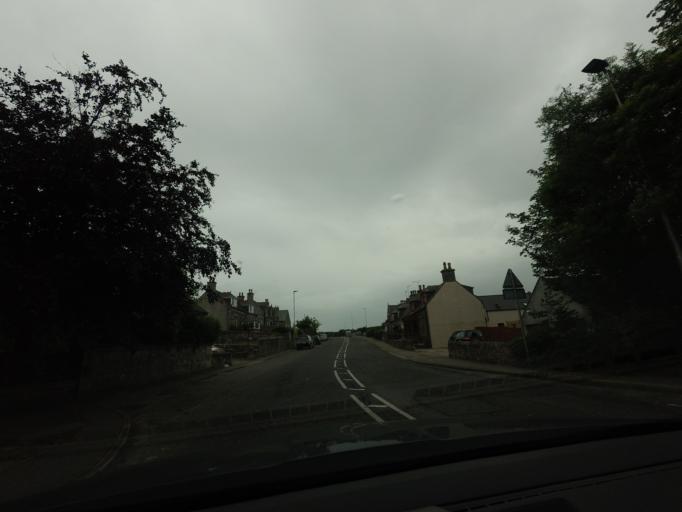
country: GB
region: Scotland
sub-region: Aberdeenshire
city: Portsoy
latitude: 57.6783
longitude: -2.6878
